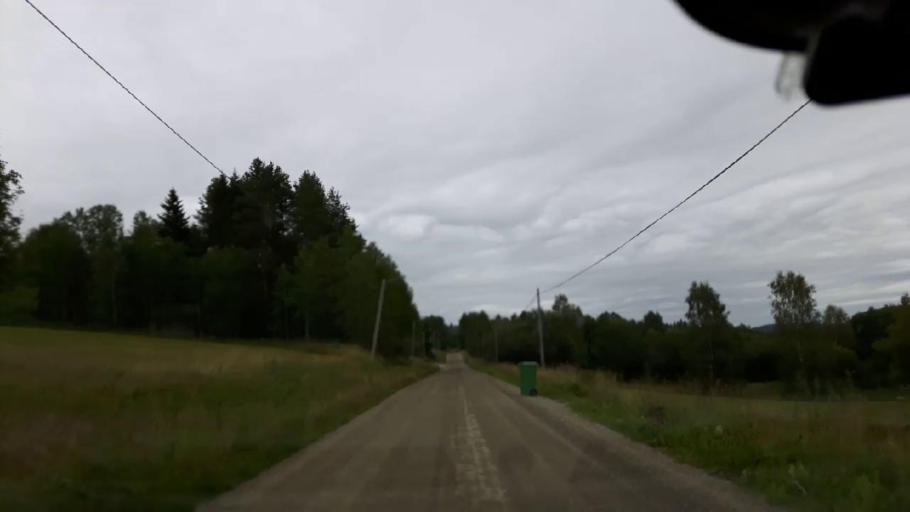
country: SE
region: Jaemtland
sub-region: Braecke Kommun
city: Braecke
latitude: 63.0333
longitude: 15.3676
